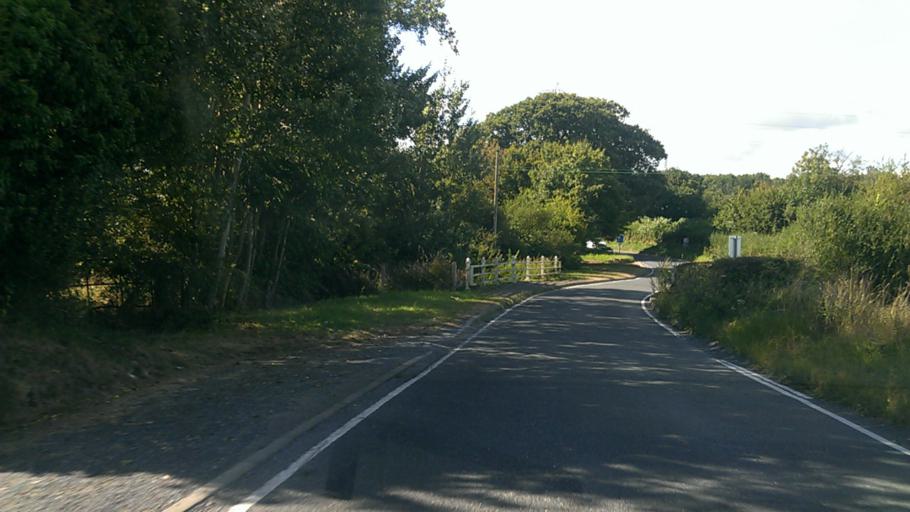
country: GB
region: England
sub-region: Essex
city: Layer de la Haye
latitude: 51.8426
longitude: 0.8896
